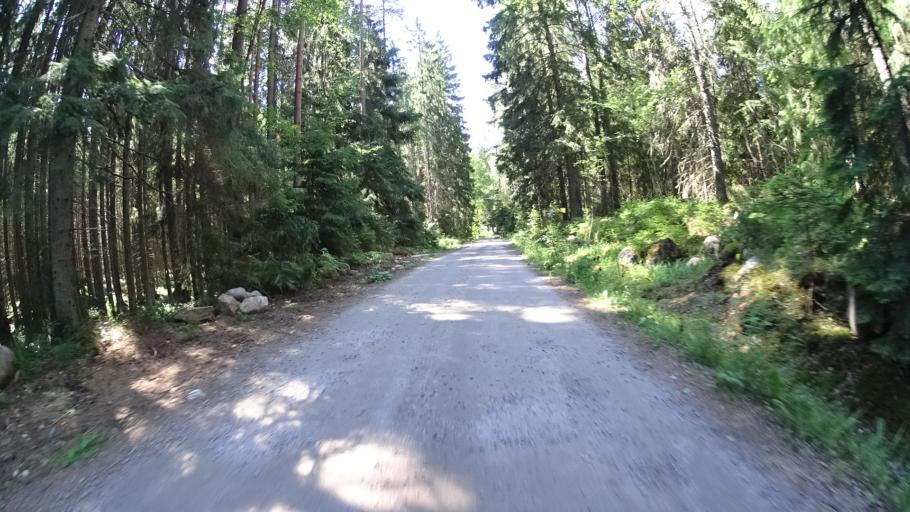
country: FI
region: Uusimaa
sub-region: Helsinki
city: Vihti
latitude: 60.3131
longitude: 24.4467
